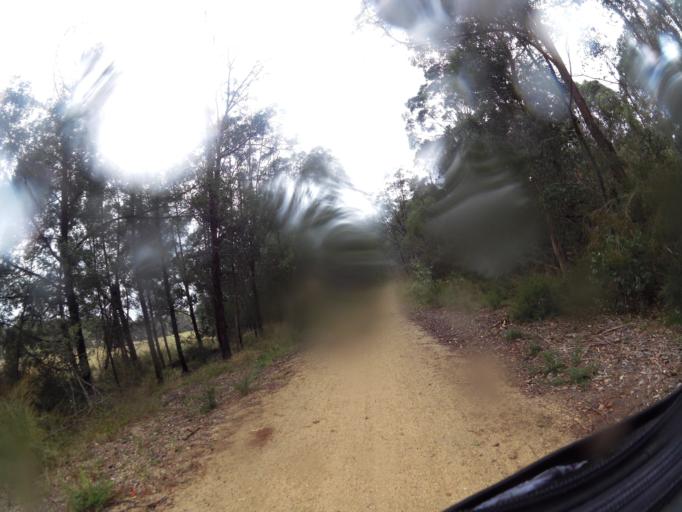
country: AU
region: Victoria
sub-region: East Gippsland
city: Bairnsdale
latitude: -37.7482
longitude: 147.8111
